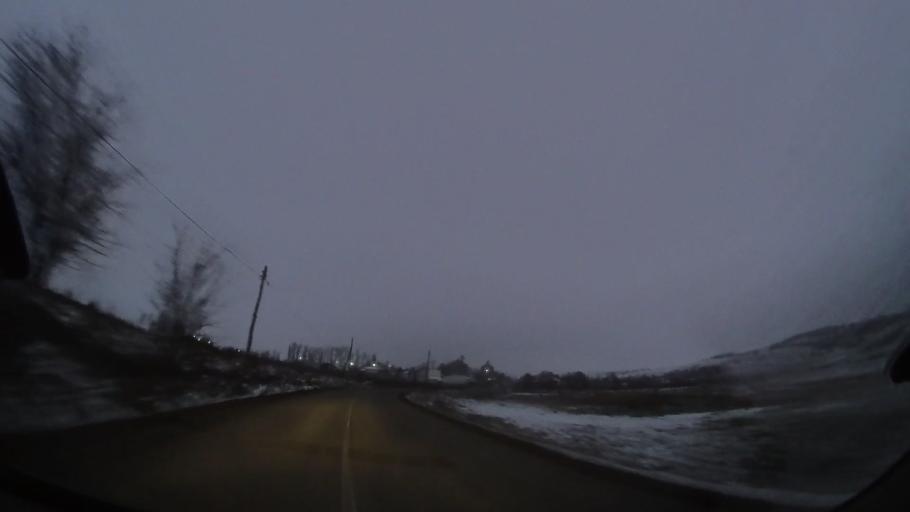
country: RO
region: Vaslui
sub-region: Comuna Dimitrie Cantemir
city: Dimitrie Cantemir
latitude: 46.4964
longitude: 28.0523
